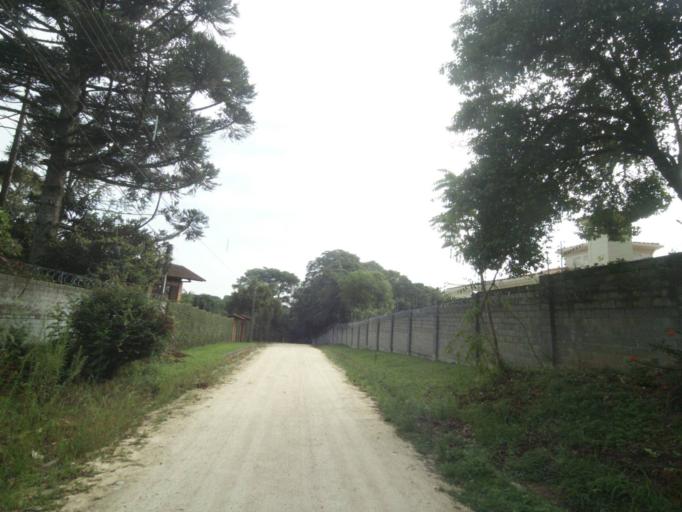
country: BR
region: Parana
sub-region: Curitiba
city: Curitiba
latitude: -25.4036
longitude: -49.3111
